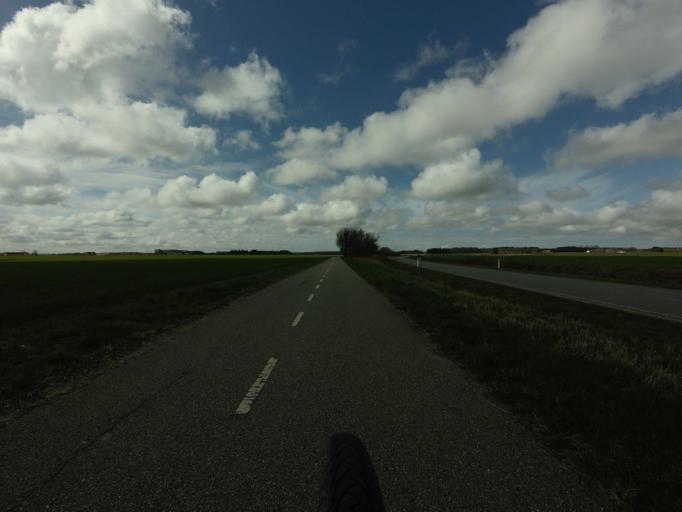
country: DK
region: North Denmark
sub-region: Hjorring Kommune
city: Vra
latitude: 57.3532
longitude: 9.9012
